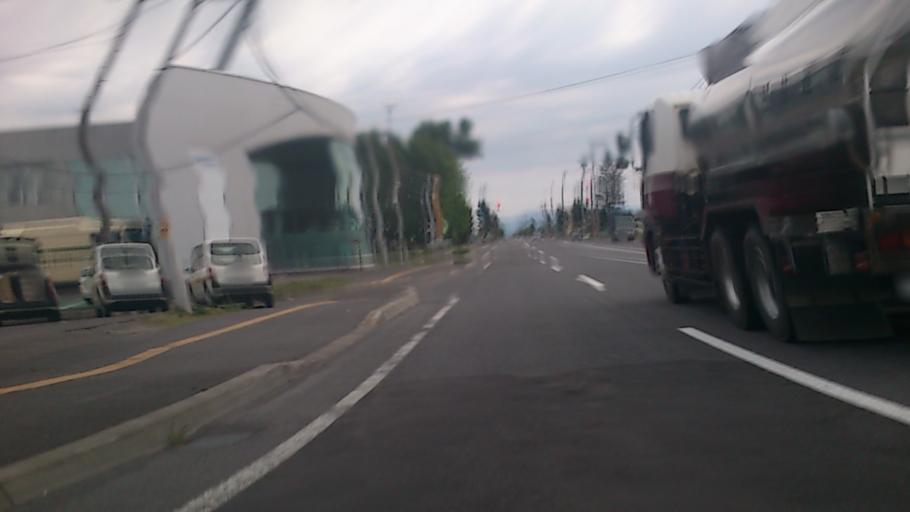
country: JP
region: Hokkaido
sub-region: Asahikawa-shi
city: Asahikawa
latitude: 43.8188
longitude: 142.4471
